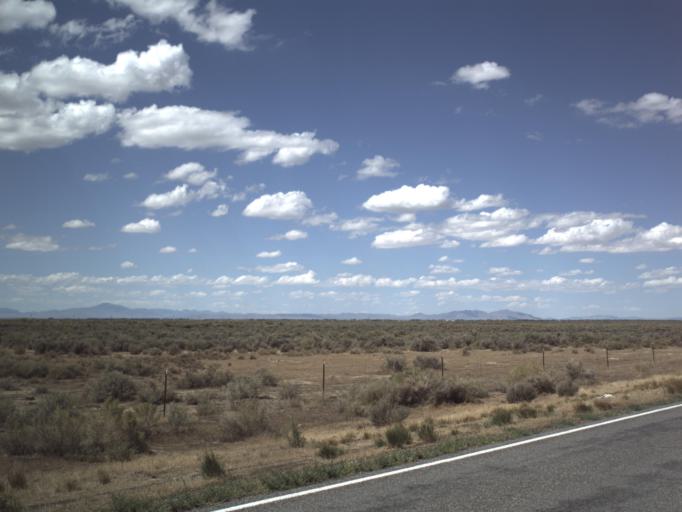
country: US
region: Utah
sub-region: Millard County
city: Delta
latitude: 39.2515
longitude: -112.4400
